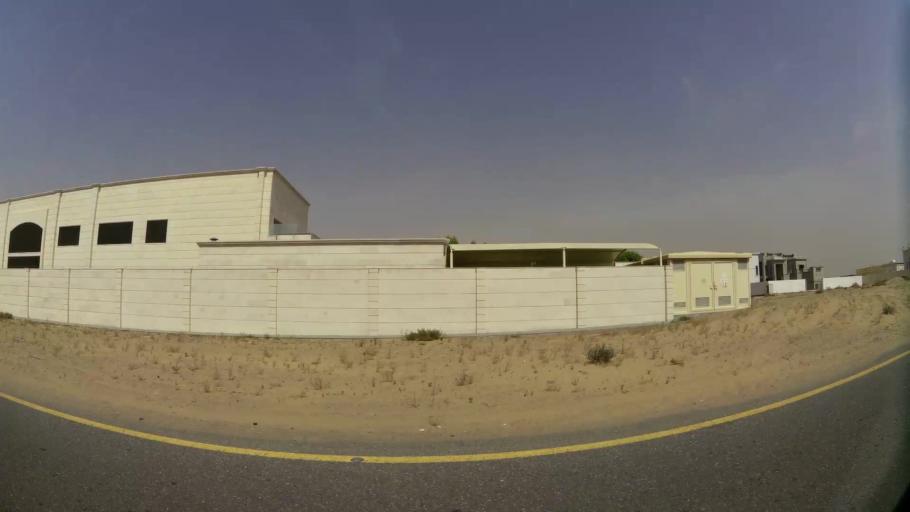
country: AE
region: Ash Shariqah
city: Sharjah
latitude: 25.2449
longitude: 55.4926
